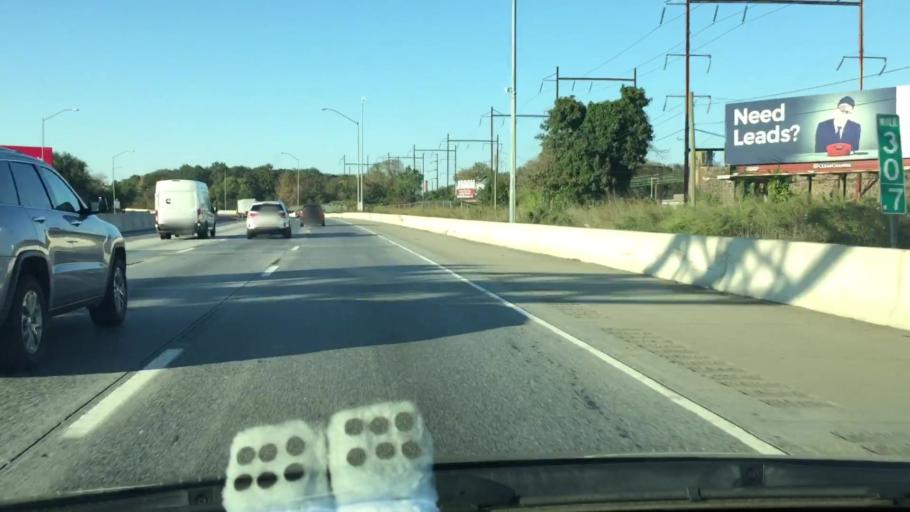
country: US
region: New Jersey
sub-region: Burlington County
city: Riverton
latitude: 40.0341
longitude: -75.0155
